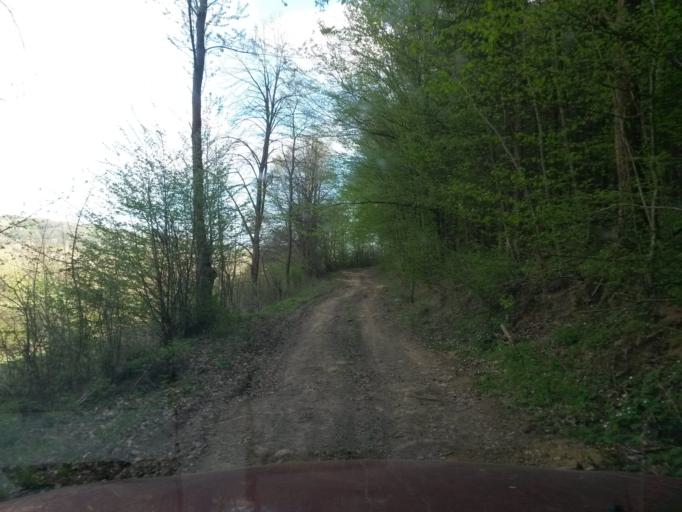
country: SK
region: Presovsky
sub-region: Okres Presov
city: Presov
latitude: 48.9530
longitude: 21.1530
